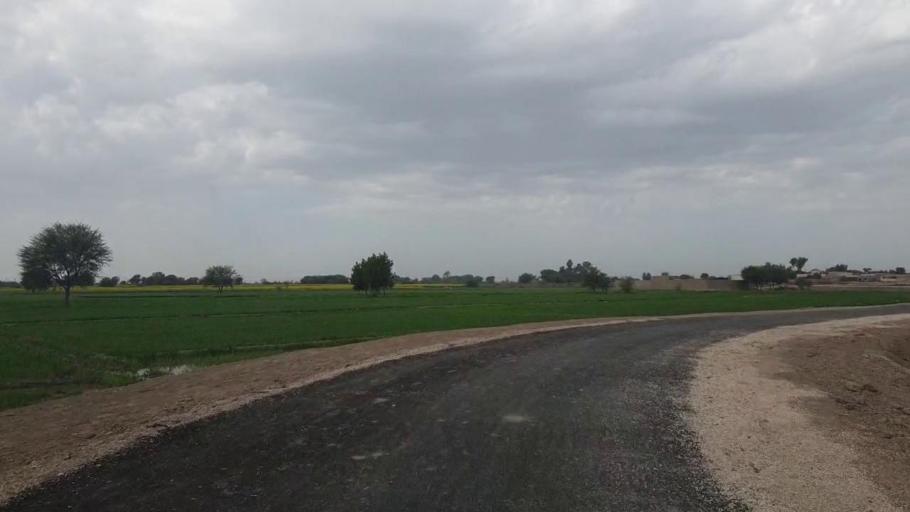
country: PK
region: Sindh
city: Hala
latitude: 25.9758
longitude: 68.3995
